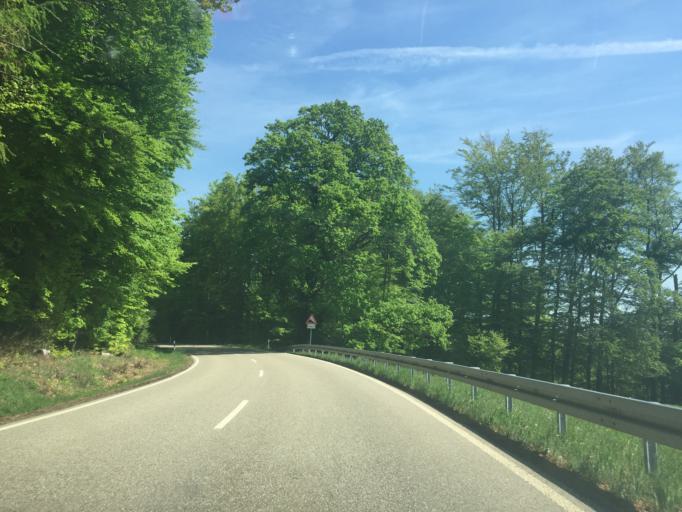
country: DE
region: Baden-Wuerttemberg
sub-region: Karlsruhe Region
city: Malsch
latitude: 48.8533
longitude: 8.3645
